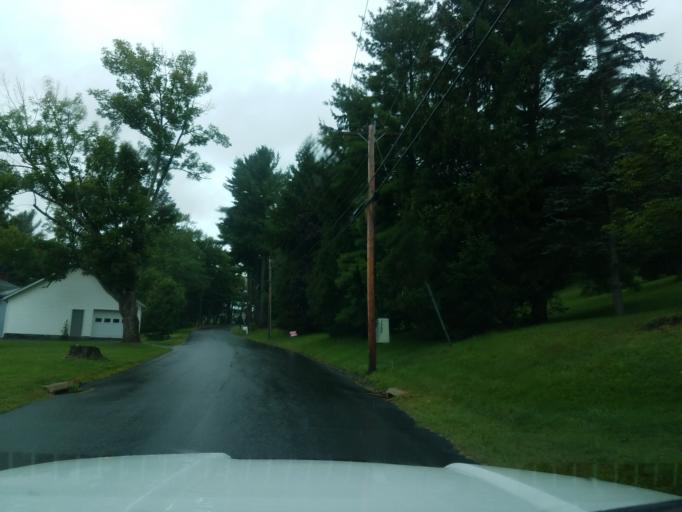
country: US
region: Connecticut
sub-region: Litchfield County
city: Canaan
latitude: 41.9632
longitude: -73.4511
